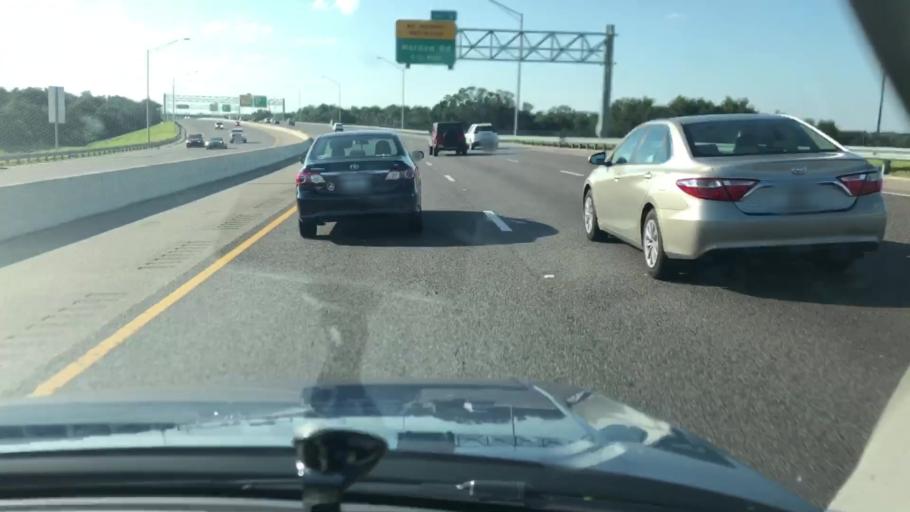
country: US
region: Florida
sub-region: Orange County
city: South Apopka
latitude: 28.6410
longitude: -81.4977
